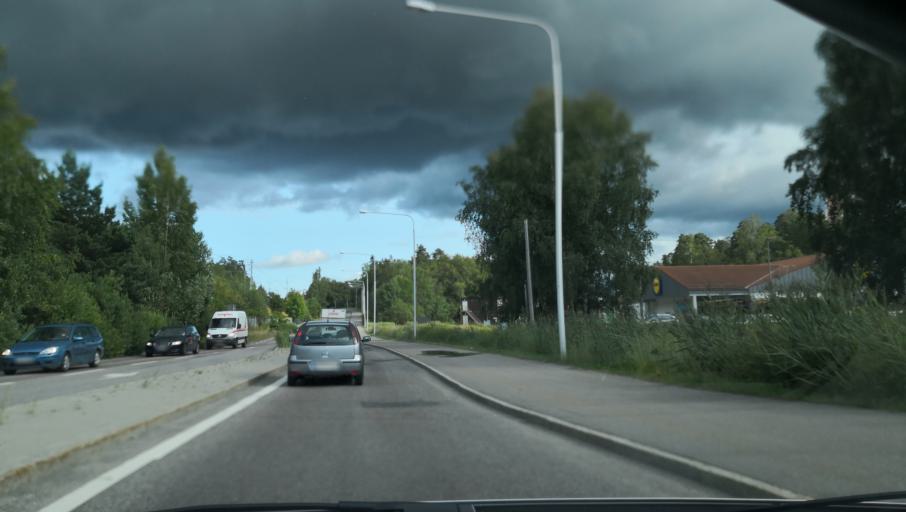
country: SE
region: Stockholm
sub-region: Stockholms Kommun
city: Arsta
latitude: 59.2477
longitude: 18.0653
